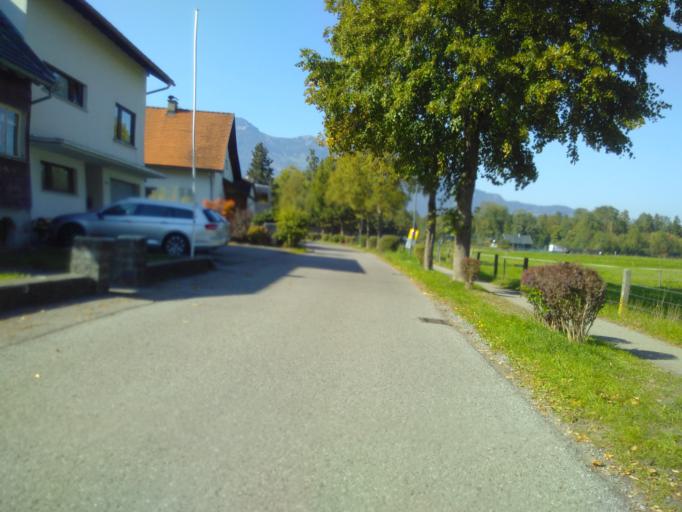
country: AT
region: Vorarlberg
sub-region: Politischer Bezirk Feldkirch
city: Nofels
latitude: 47.2571
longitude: 9.5753
